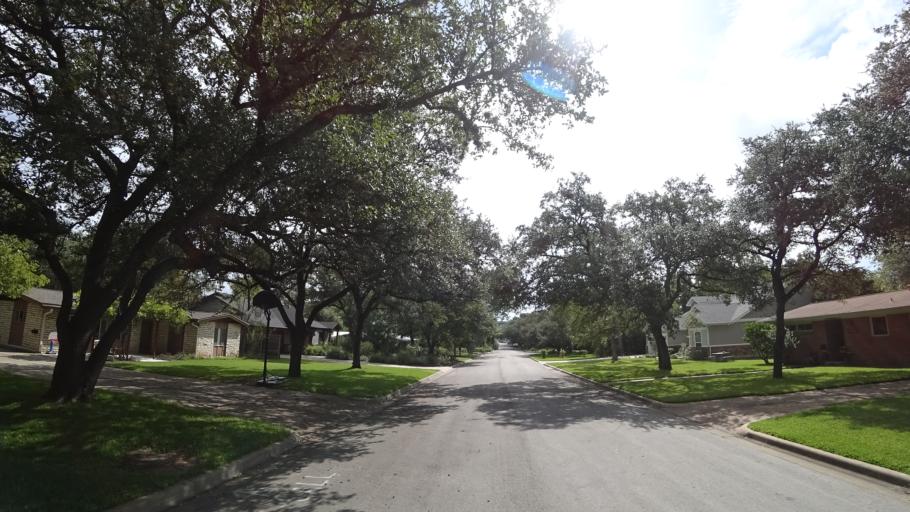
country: US
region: Texas
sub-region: Travis County
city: West Lake Hills
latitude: 30.3444
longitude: -97.7418
